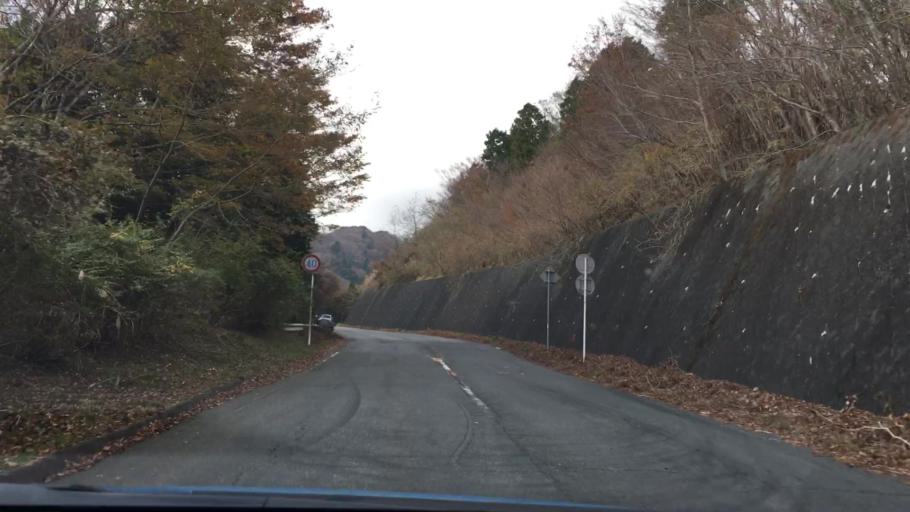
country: JP
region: Shizuoka
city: Gotemba
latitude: 35.4000
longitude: 138.9344
